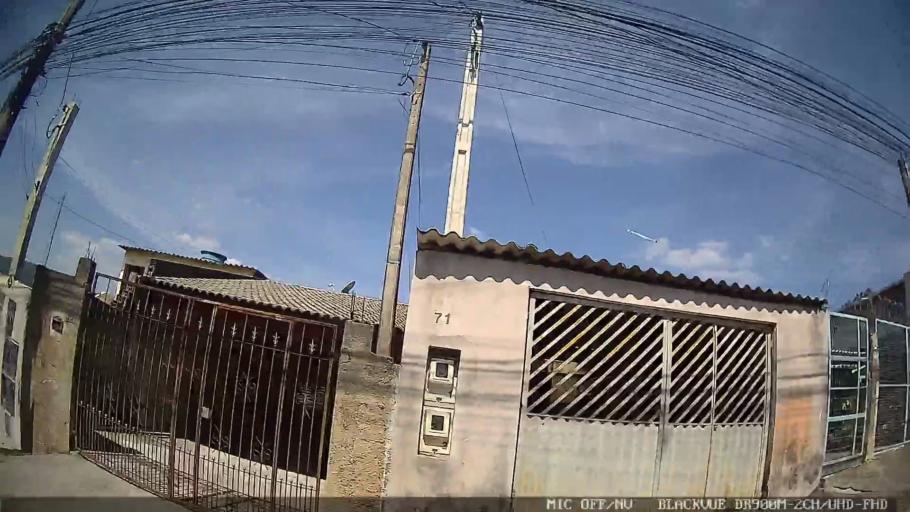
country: BR
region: Sao Paulo
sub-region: Cabreuva
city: Cabreuva
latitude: -23.2722
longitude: -47.0547
